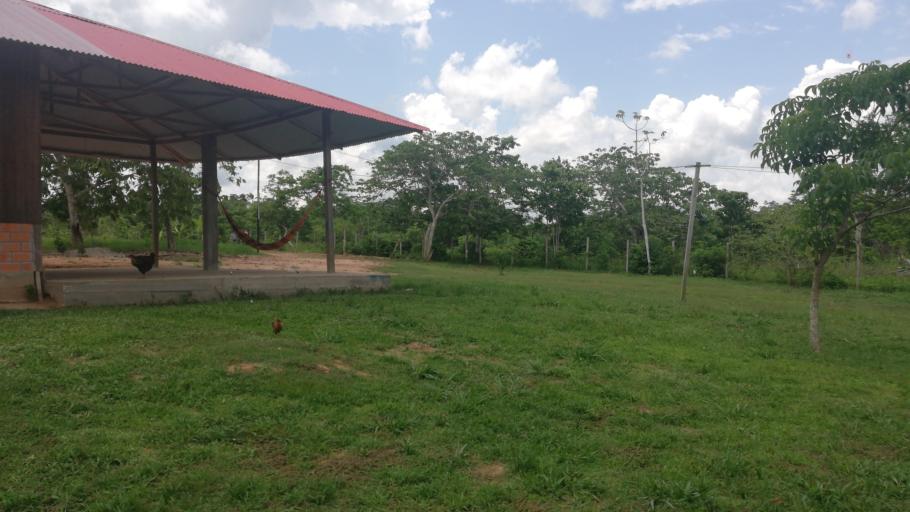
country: PE
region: Ucayali
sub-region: Provincia de Coronel Portillo
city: Puerto Callao
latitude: -8.2709
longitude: -74.6461
